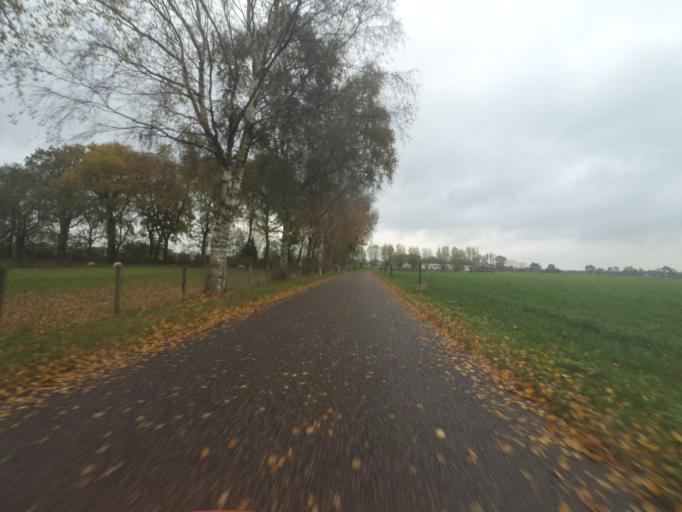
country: NL
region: Gelderland
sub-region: Gemeente Ede
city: Ederveen
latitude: 52.0849
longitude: 5.5670
